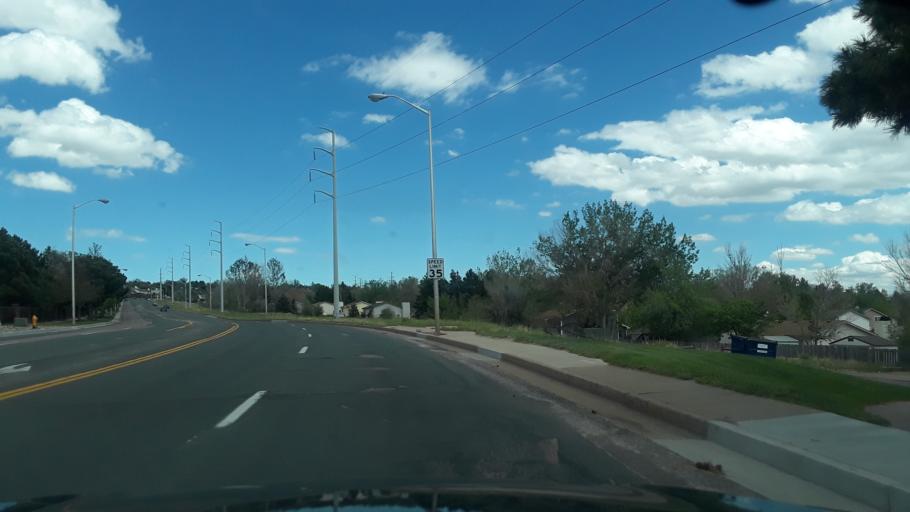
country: US
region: Colorado
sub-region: El Paso County
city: Air Force Academy
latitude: 38.9443
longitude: -104.7919
